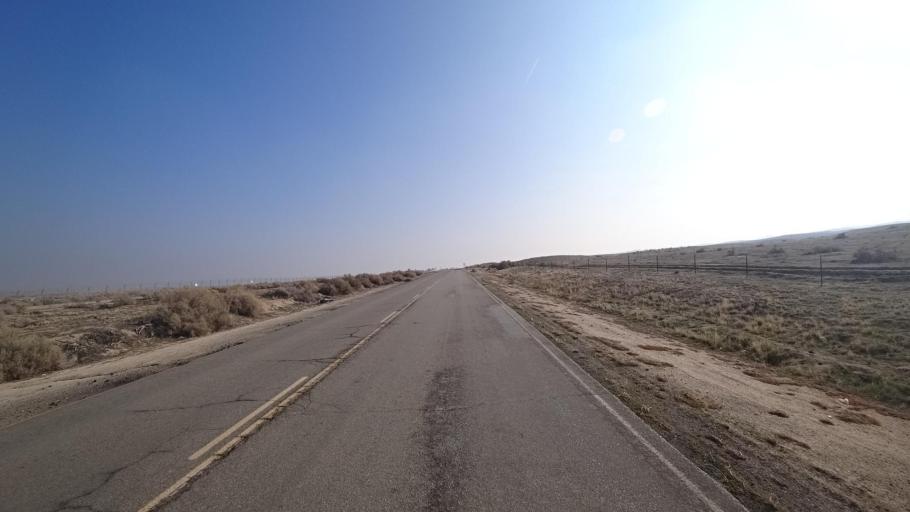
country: US
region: California
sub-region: Kern County
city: Buttonwillow
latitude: 35.3035
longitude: -119.3651
